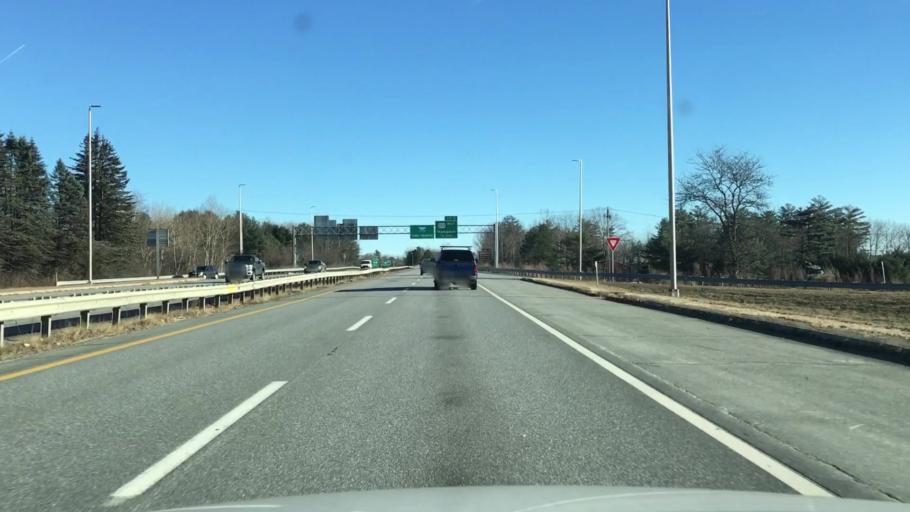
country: US
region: Maine
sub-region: Penobscot County
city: Bangor
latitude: 44.7865
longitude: -68.8049
